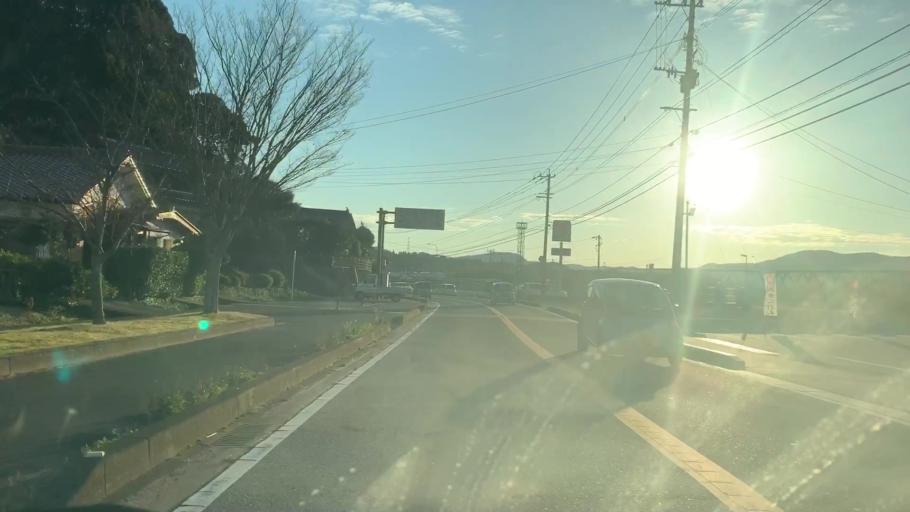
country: JP
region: Saga Prefecture
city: Karatsu
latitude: 33.3568
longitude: 130.0059
